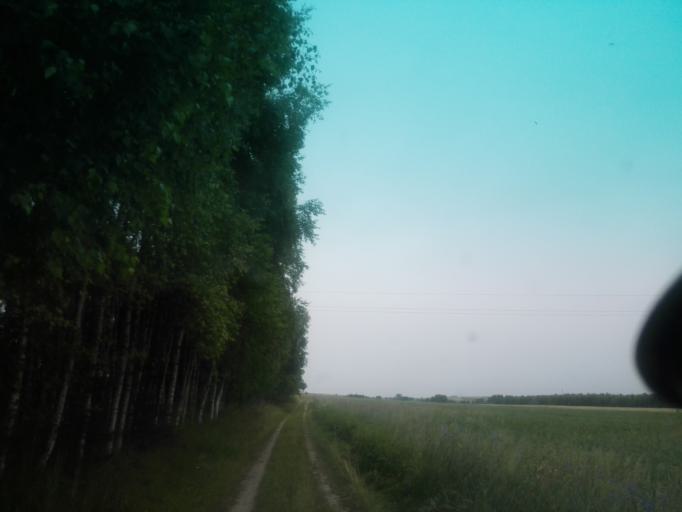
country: PL
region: Silesian Voivodeship
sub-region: Powiat czestochowski
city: Mstow
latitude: 50.7877
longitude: 19.3609
